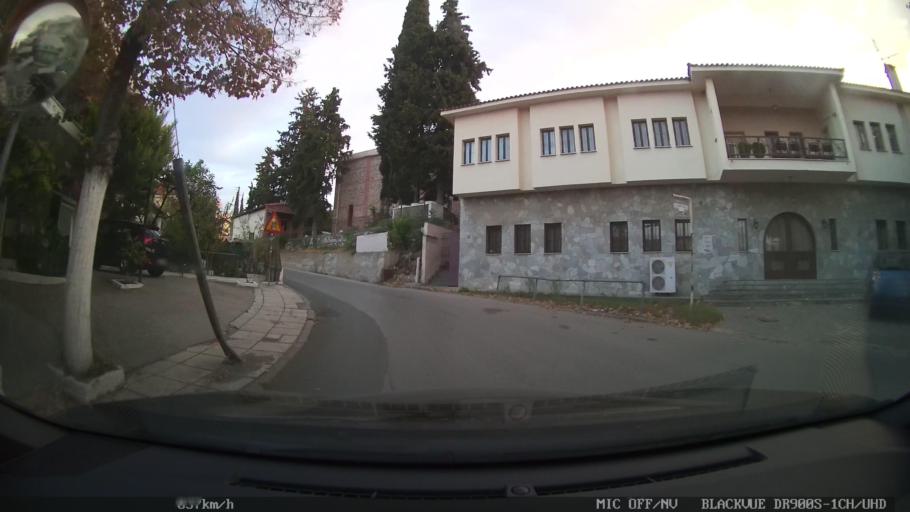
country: GR
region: Central Macedonia
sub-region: Nomos Thessalonikis
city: Pylaia
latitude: 40.6018
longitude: 22.9898
